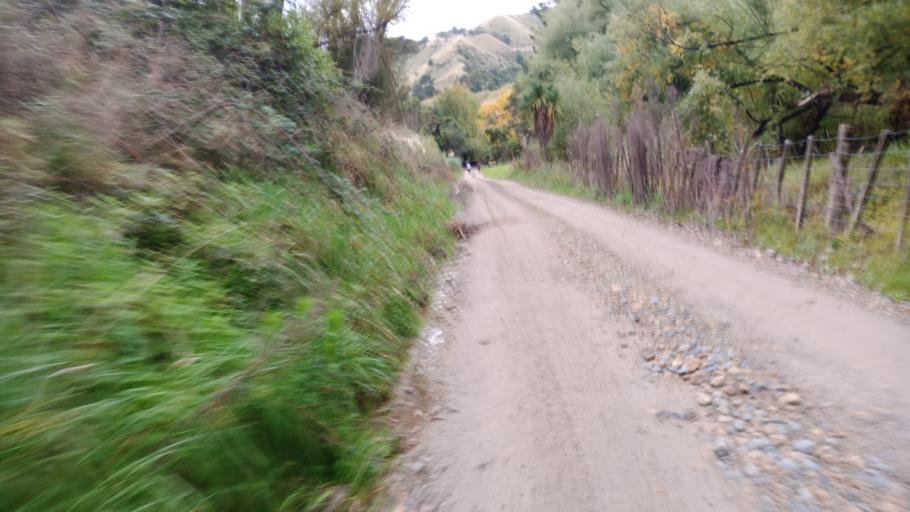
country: NZ
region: Gisborne
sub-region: Gisborne District
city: Gisborne
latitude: -38.6466
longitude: 178.0441
